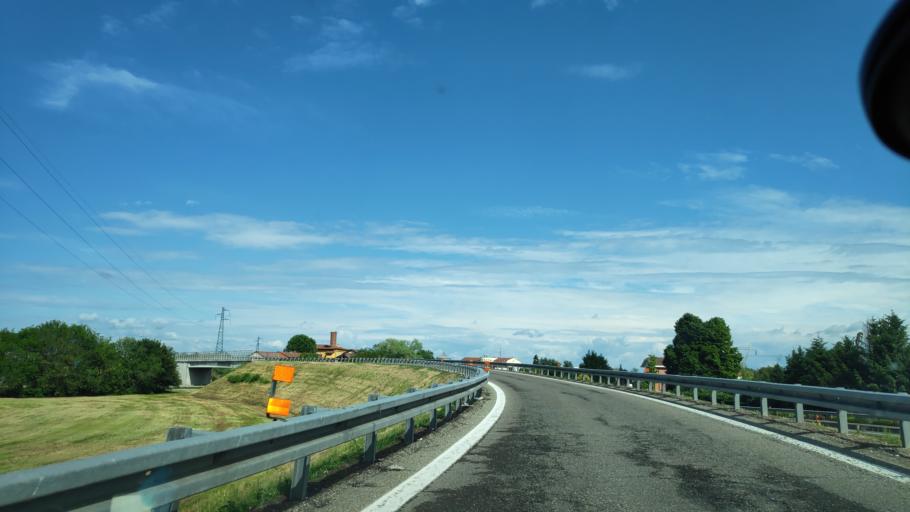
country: IT
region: Piedmont
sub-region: Provincia di Torino
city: Cambiano
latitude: 44.9587
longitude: 7.7816
